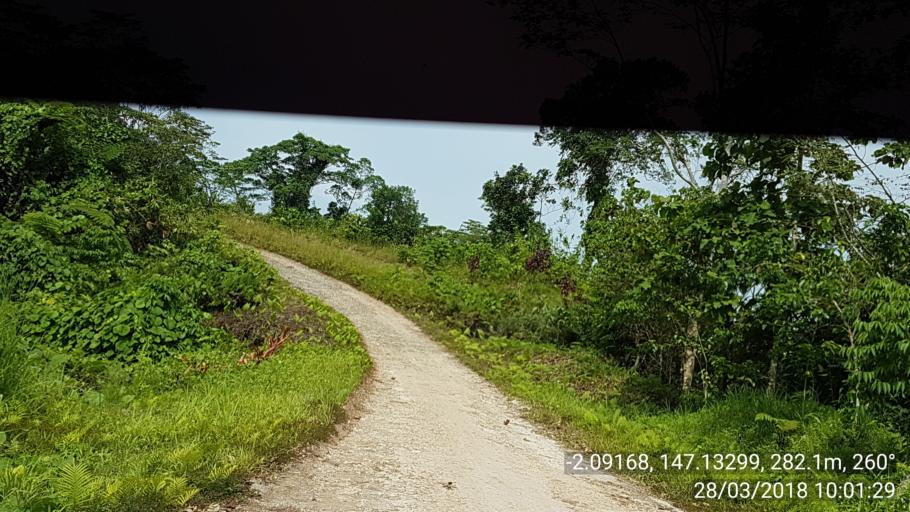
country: PG
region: Manus
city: Lorengau
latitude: -2.0917
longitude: 147.1331
